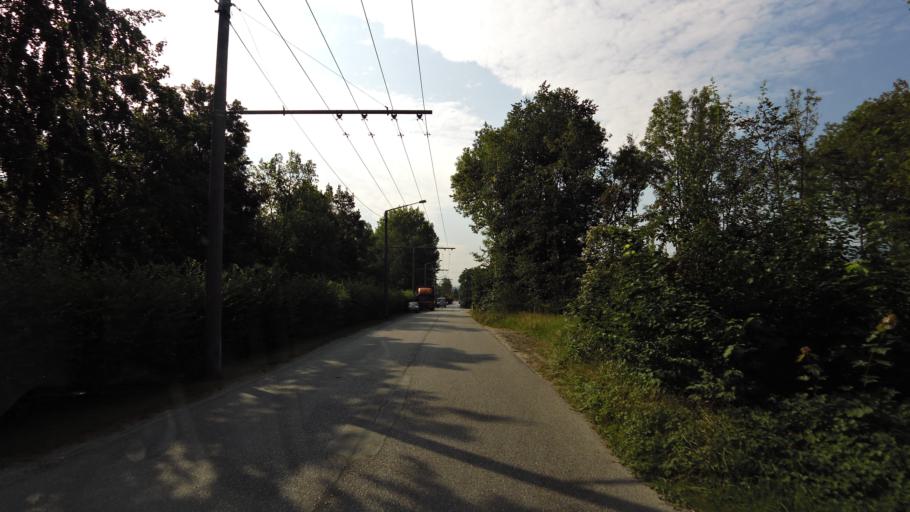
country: AT
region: Salzburg
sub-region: Politischer Bezirk Salzburg-Umgebung
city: Bergheim
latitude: 47.8343
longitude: 13.0173
